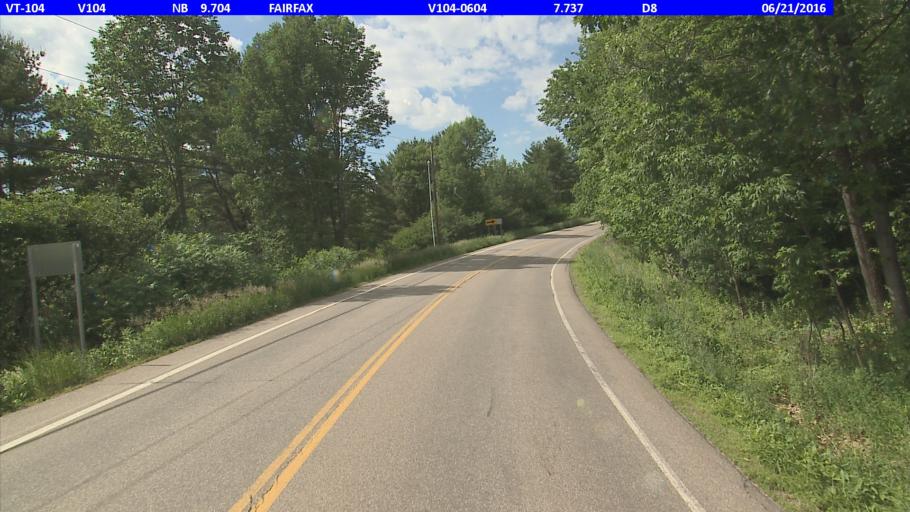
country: US
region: Vermont
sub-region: Chittenden County
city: Milton
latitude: 44.6959
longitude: -73.0366
